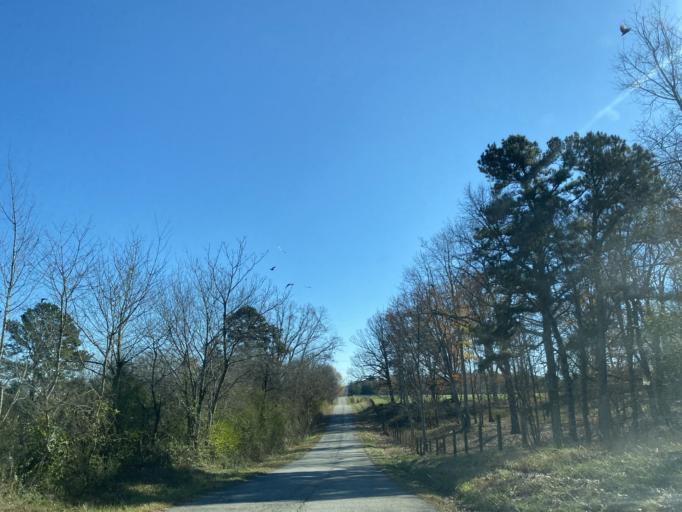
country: US
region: South Carolina
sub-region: Spartanburg County
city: Mayo
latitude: 35.1364
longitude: -81.7672
